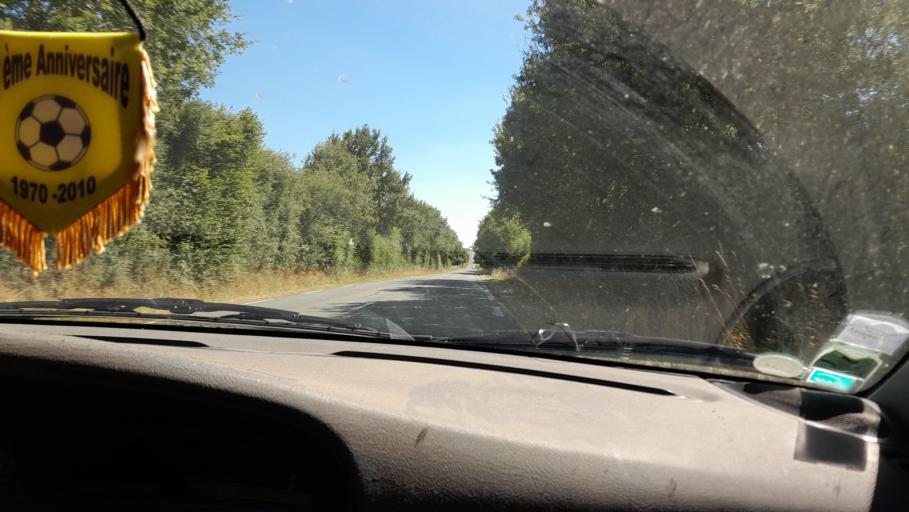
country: FR
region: Pays de la Loire
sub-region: Departement de la Loire-Atlantique
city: Saint-Mars-la-Jaille
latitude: 47.5660
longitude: -1.1875
